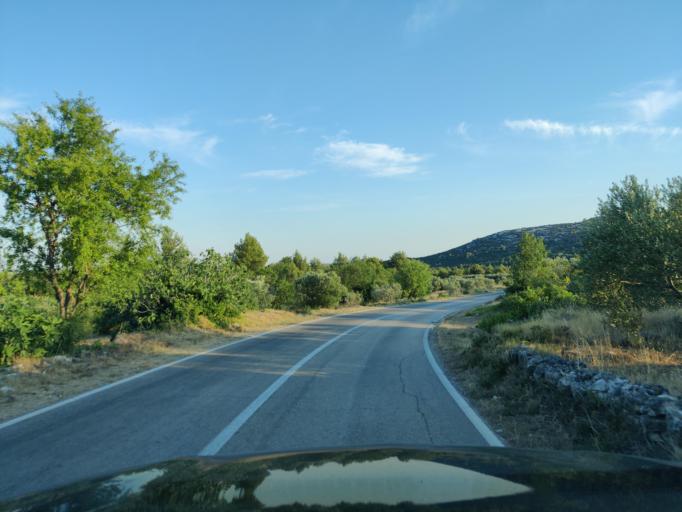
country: HR
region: Sibensko-Kniniska
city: Tribunj
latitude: 43.7774
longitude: 15.7278
